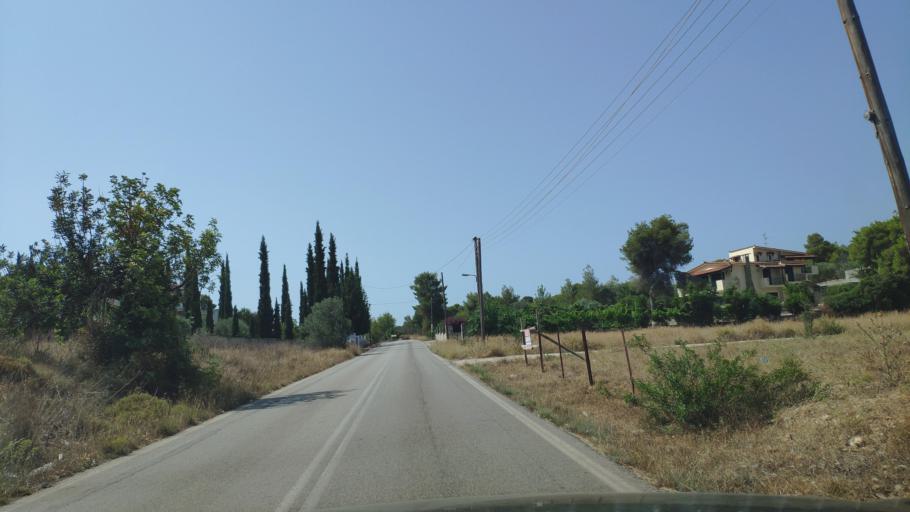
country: GR
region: Peloponnese
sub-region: Nomos Argolidos
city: Porto Cheli
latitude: 37.3043
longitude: 23.1647
